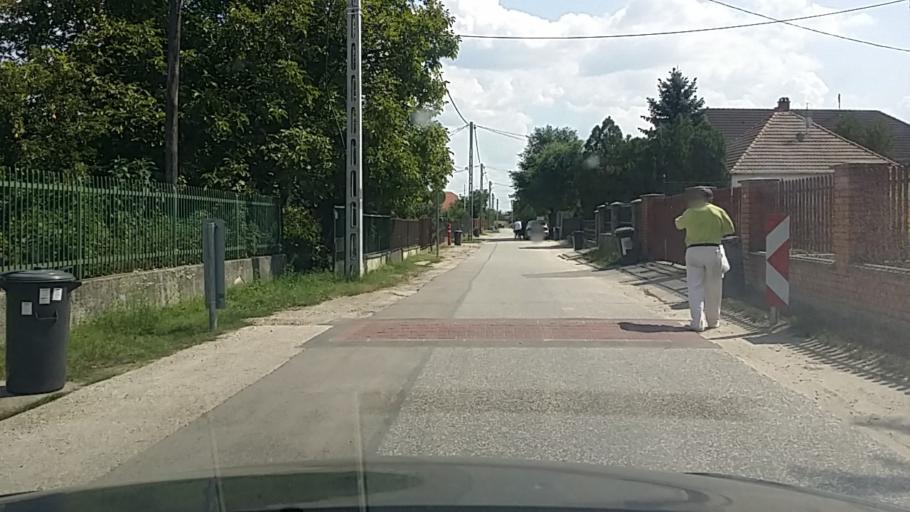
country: HU
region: Pest
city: Halasztelek
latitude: 47.3798
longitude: 19.0132
